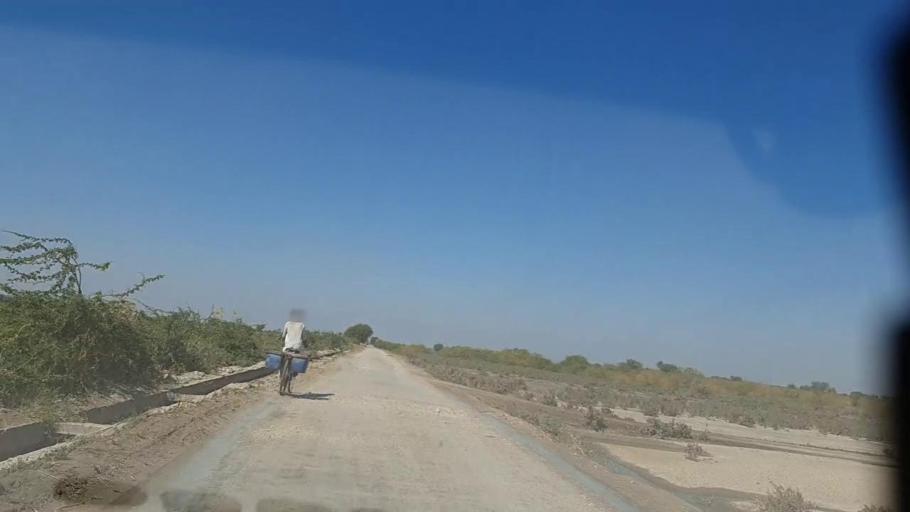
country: PK
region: Sindh
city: Digri
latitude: 25.1702
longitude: 69.0633
